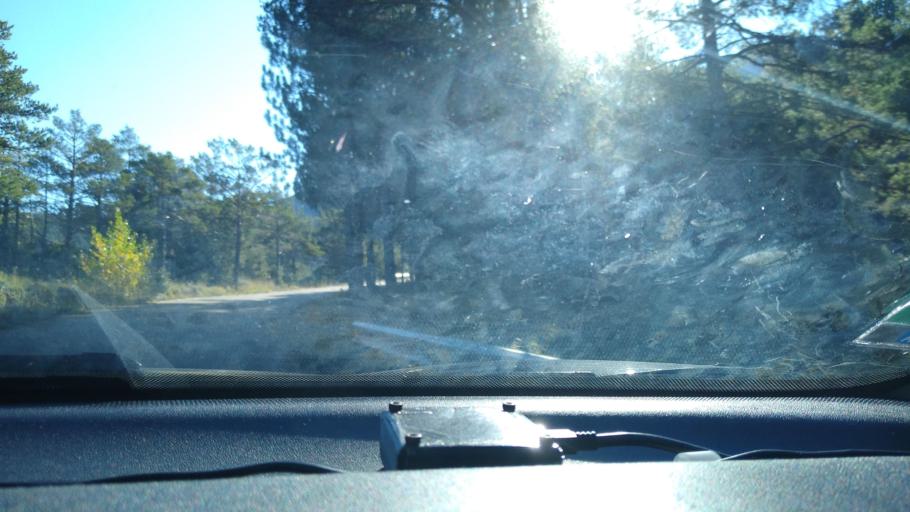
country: ES
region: Catalonia
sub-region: Provincia de Barcelona
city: Saldes
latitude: 42.2103
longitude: 1.7211
